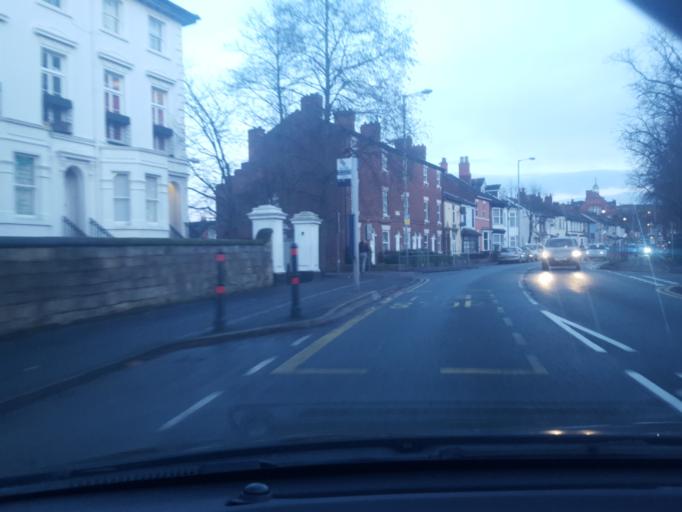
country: GB
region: England
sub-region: Wolverhampton
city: Wolverhampton
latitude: 52.5921
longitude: -2.1375
